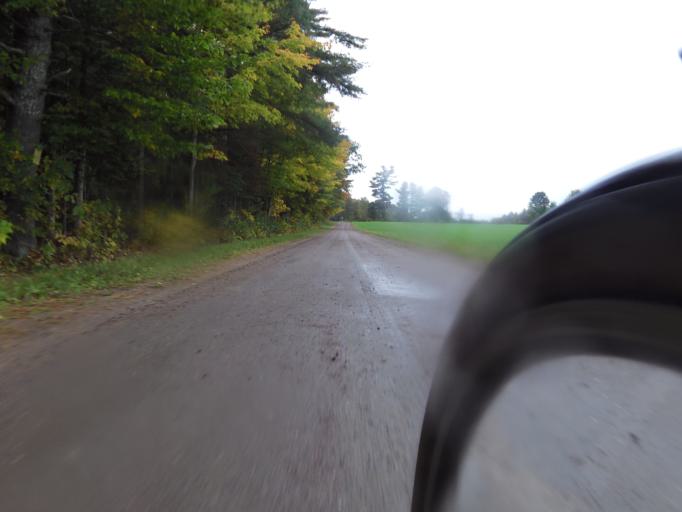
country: CA
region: Quebec
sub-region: Outaouais
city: Shawville
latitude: 45.6794
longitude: -76.5463
